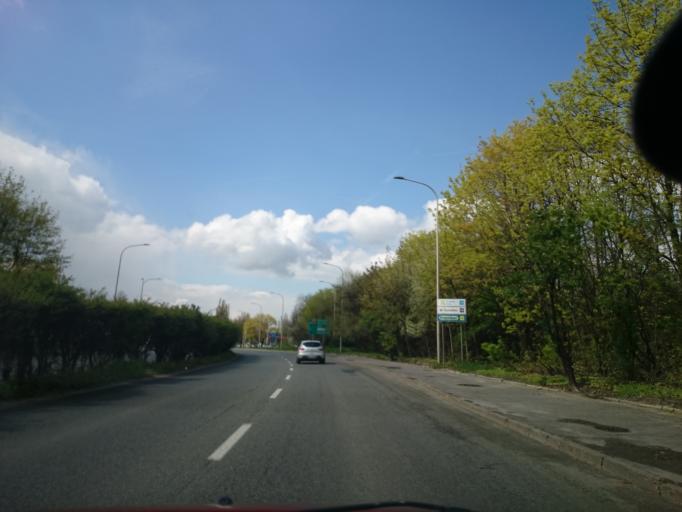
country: PL
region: Opole Voivodeship
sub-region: Powiat opolski
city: Opole
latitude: 50.6736
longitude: 17.9355
